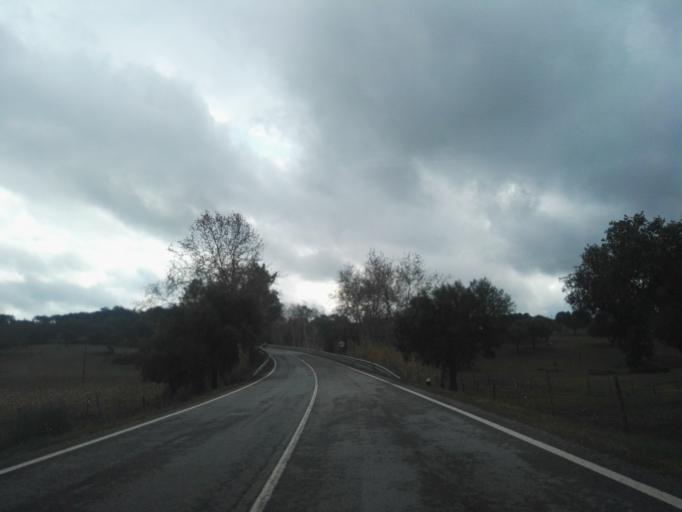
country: PT
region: Portalegre
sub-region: Arronches
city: Arronches
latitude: 39.0905
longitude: -7.2837
